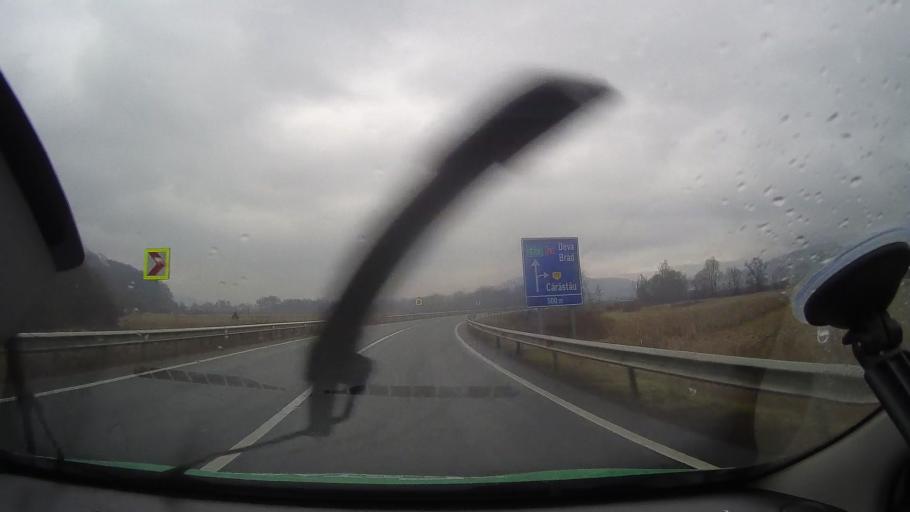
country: RO
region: Hunedoara
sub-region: Comuna Tomesti
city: Tomesti
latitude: 46.1840
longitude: 22.6571
